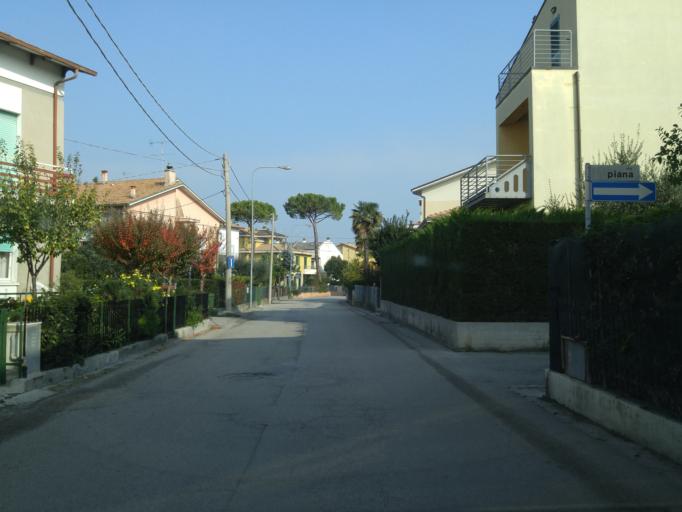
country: IT
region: The Marches
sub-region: Provincia di Pesaro e Urbino
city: Fano
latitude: 43.8304
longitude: 13.0114
